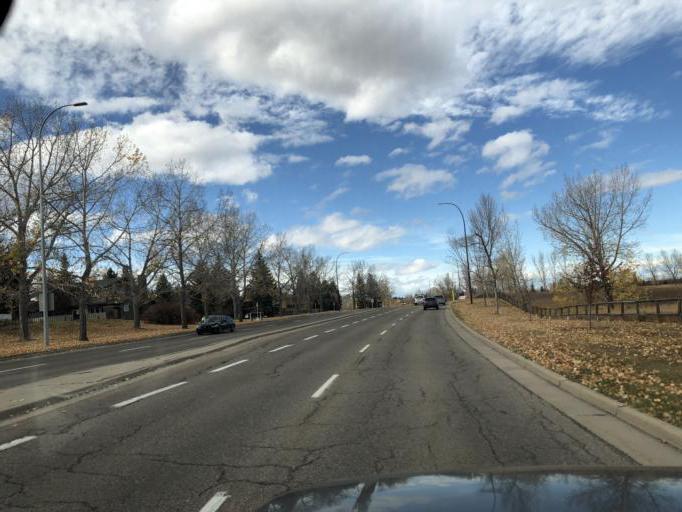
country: CA
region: Alberta
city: Calgary
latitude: 50.9733
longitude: -114.1244
